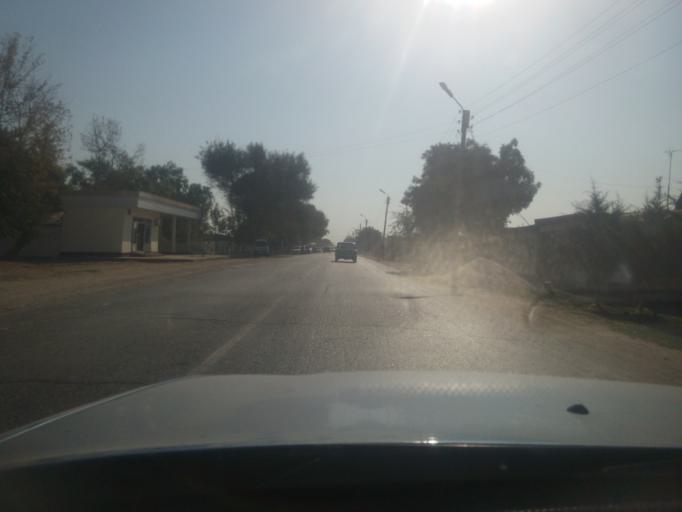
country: UZ
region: Sirdaryo
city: Guliston
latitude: 40.4946
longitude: 68.7943
